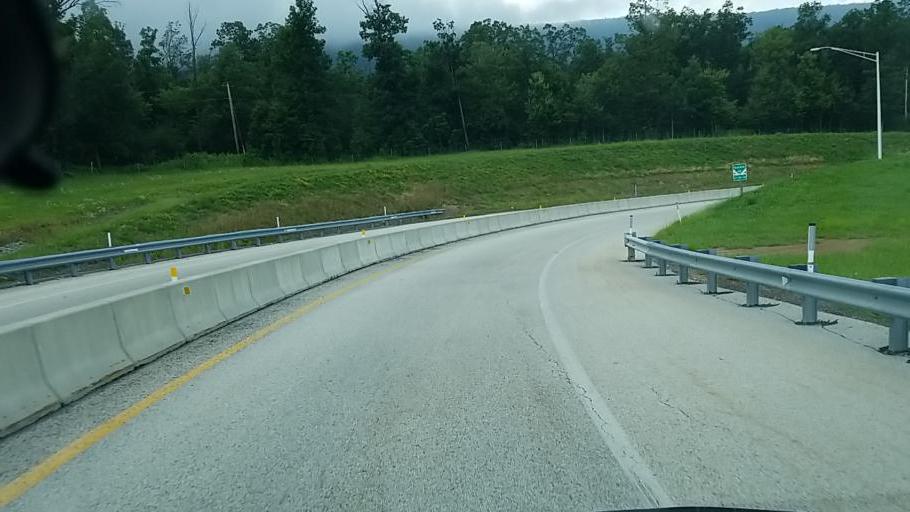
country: US
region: Pennsylvania
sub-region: Franklin County
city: Doylestown
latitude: 40.1592
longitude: -77.6147
